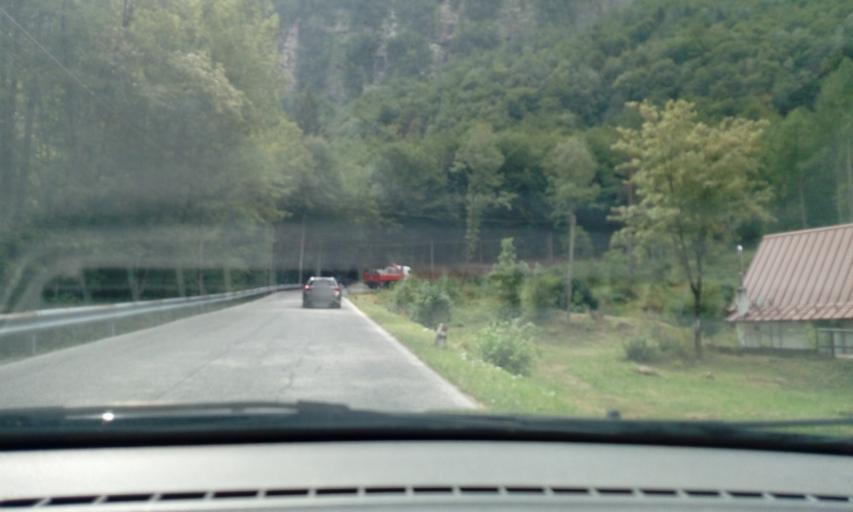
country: IT
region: Friuli Venezia Giulia
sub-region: Provincia di Udine
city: Malborghetto
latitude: 46.3955
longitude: 13.4379
